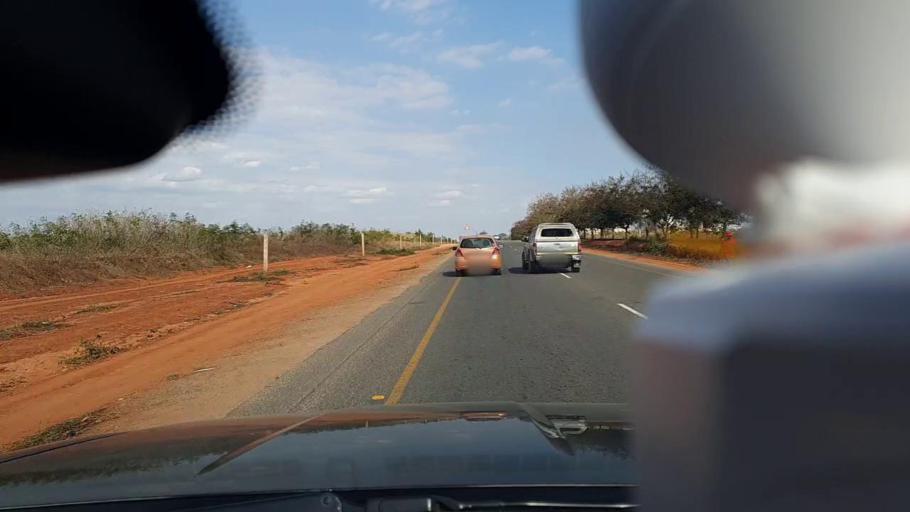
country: MZ
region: Nampula
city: Nampula
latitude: -15.1529
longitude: 39.3024
